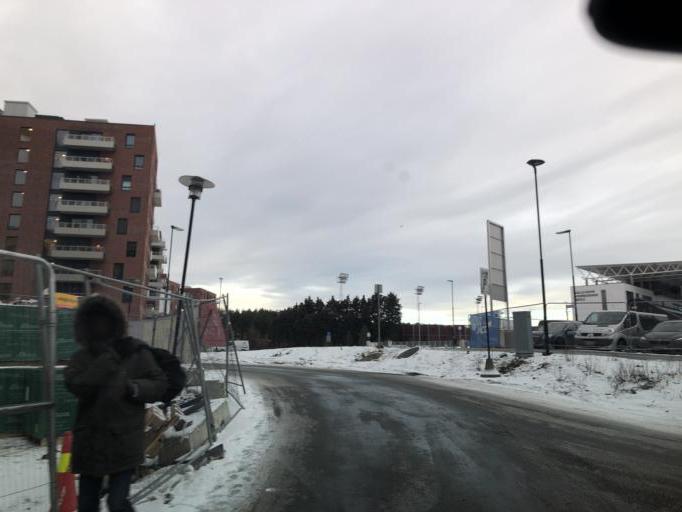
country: NO
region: Oslo
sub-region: Oslo
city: Oslo
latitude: 59.9161
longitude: 10.8049
